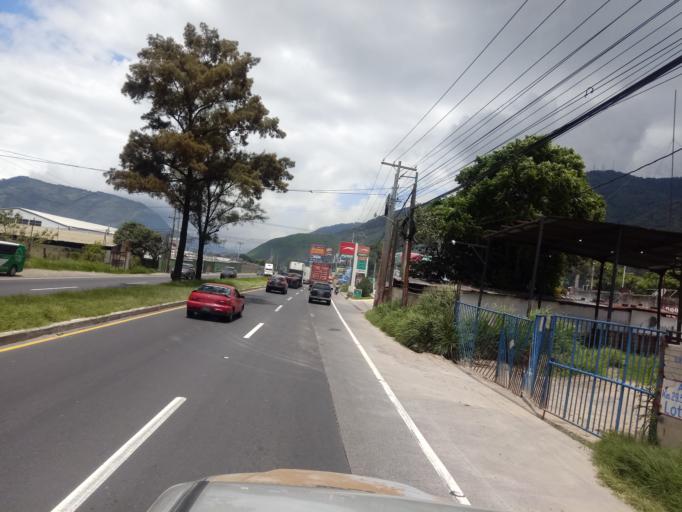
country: GT
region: Guatemala
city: Amatitlan
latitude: 14.4731
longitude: -90.6352
